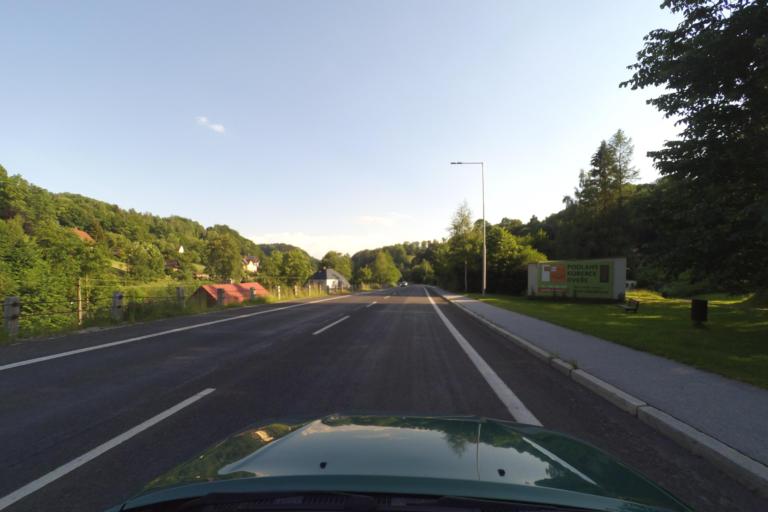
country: CZ
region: Kralovehradecky
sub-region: Okres Trutnov
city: Svoboda nad Upou
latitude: 50.6454
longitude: 15.8154
